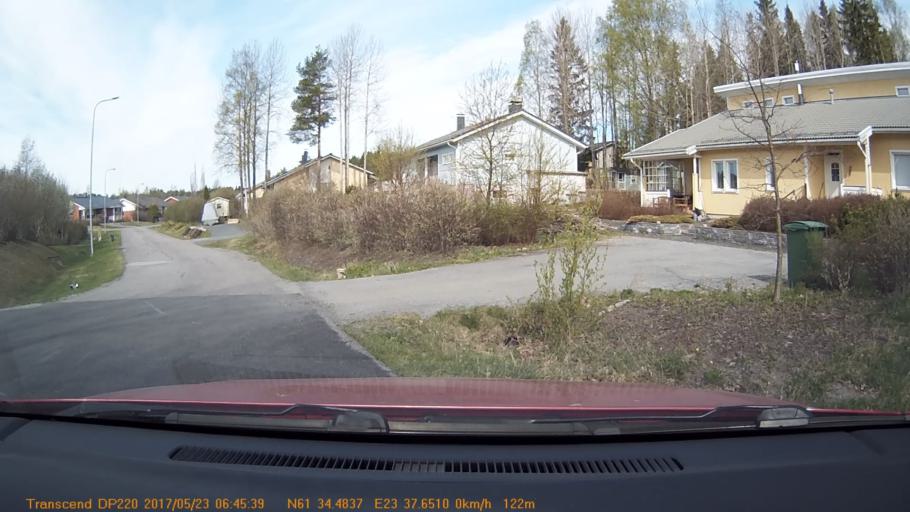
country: FI
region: Pirkanmaa
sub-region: Tampere
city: Yloejaervi
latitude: 61.5747
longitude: 23.6275
